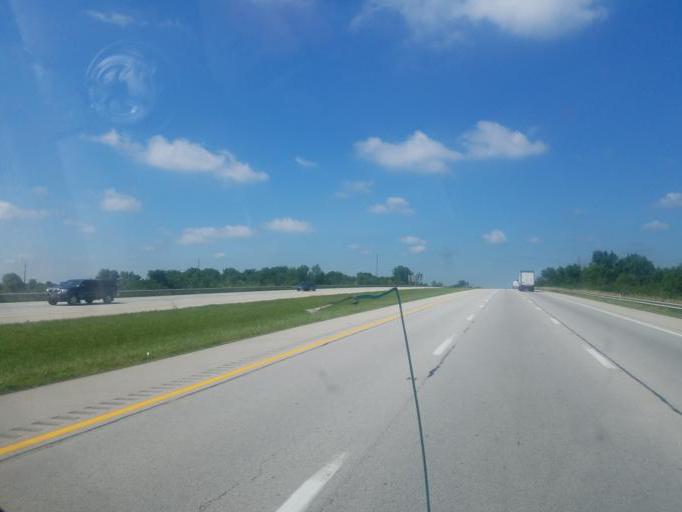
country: US
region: Ohio
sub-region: Fayette County
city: Jeffersonville
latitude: 39.6121
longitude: -83.6214
